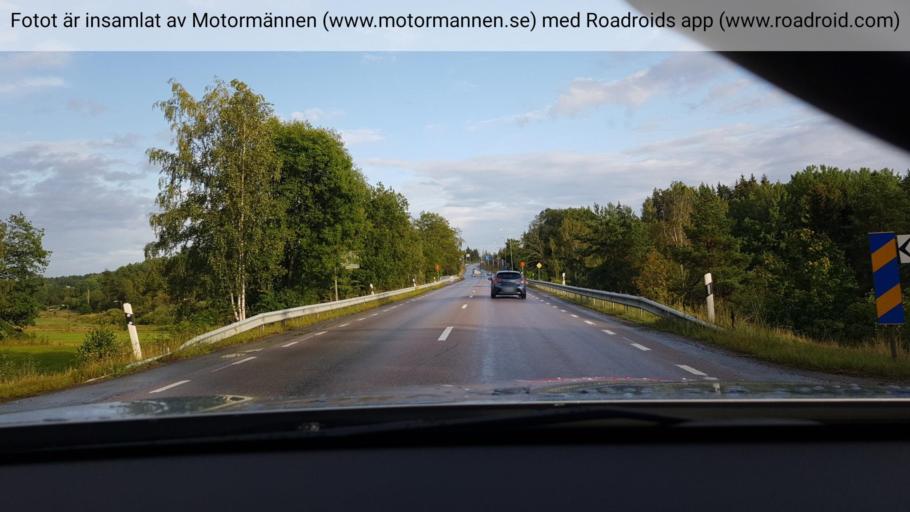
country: SE
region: Stockholm
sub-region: Norrtalje Kommun
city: Norrtalje
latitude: 59.7728
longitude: 18.6758
